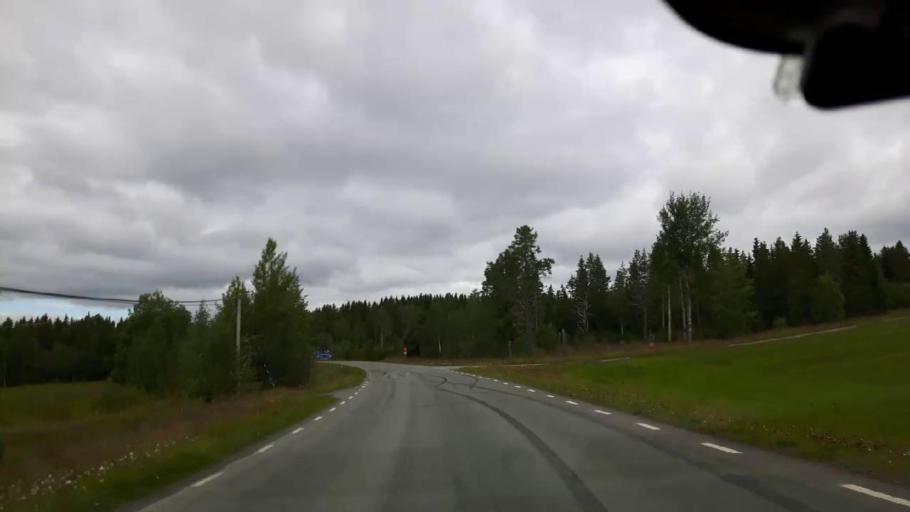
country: SE
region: Jaemtland
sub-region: Krokoms Kommun
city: Valla
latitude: 63.5065
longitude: 13.8950
